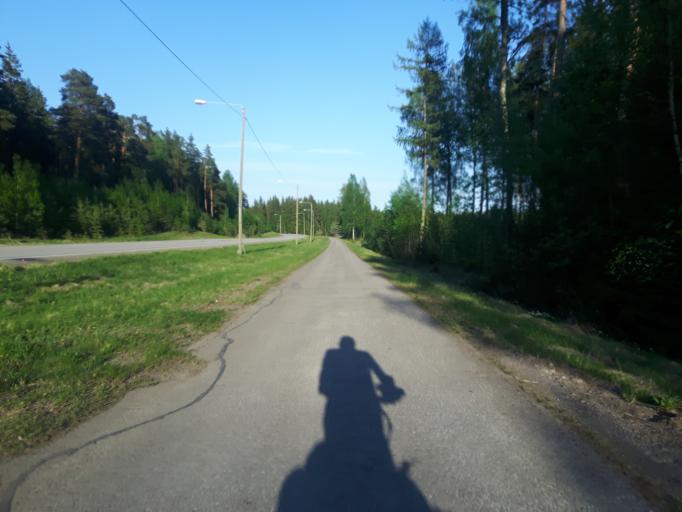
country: FI
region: Uusimaa
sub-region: Loviisa
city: Lovisa
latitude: 60.4561
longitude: 26.1457
